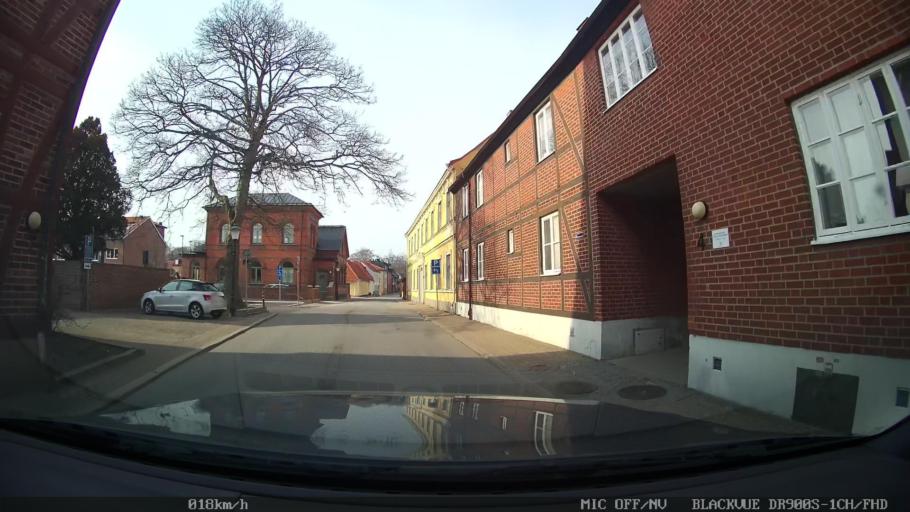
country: SE
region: Skane
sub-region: Ystads Kommun
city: Ystad
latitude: 55.4295
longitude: 13.8179
